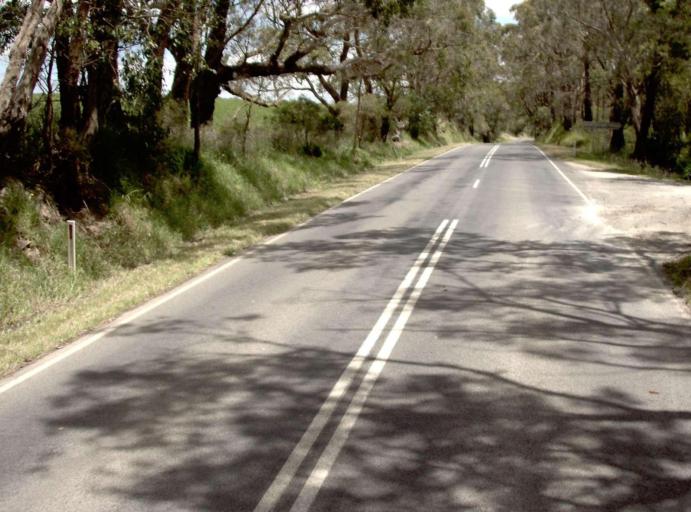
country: AU
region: Victoria
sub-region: Bass Coast
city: North Wonthaggi
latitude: -38.6773
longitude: 146.0355
